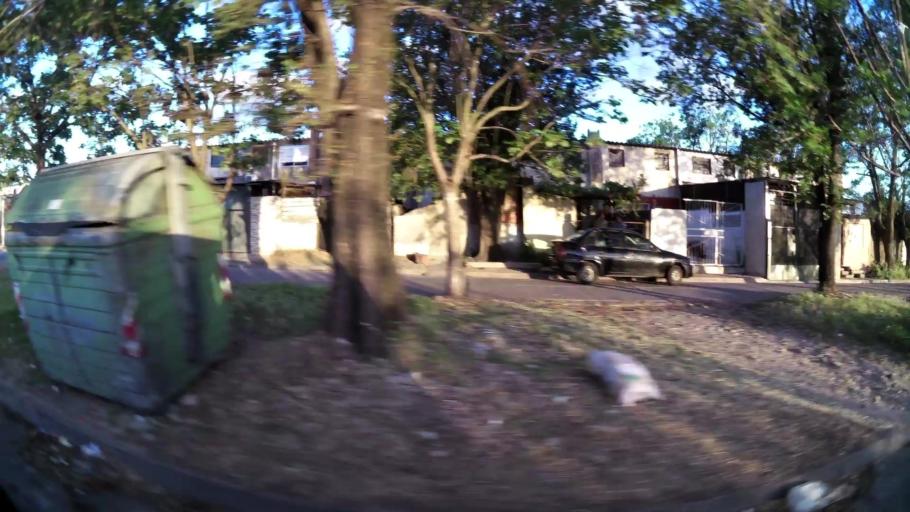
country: UY
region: Canelones
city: Paso de Carrasco
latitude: -34.8804
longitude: -56.1188
